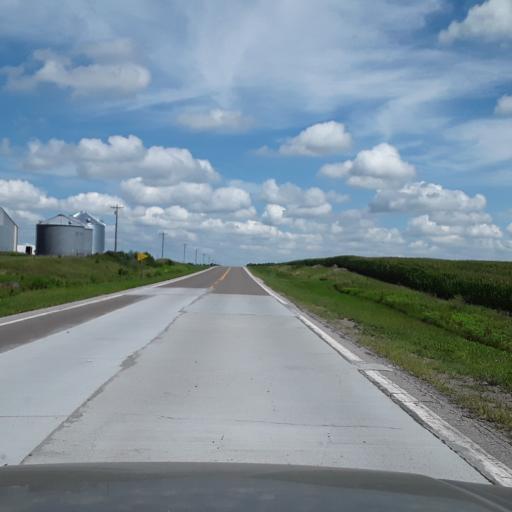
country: US
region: Nebraska
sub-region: Polk County
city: Osceola
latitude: 41.0928
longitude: -97.4259
